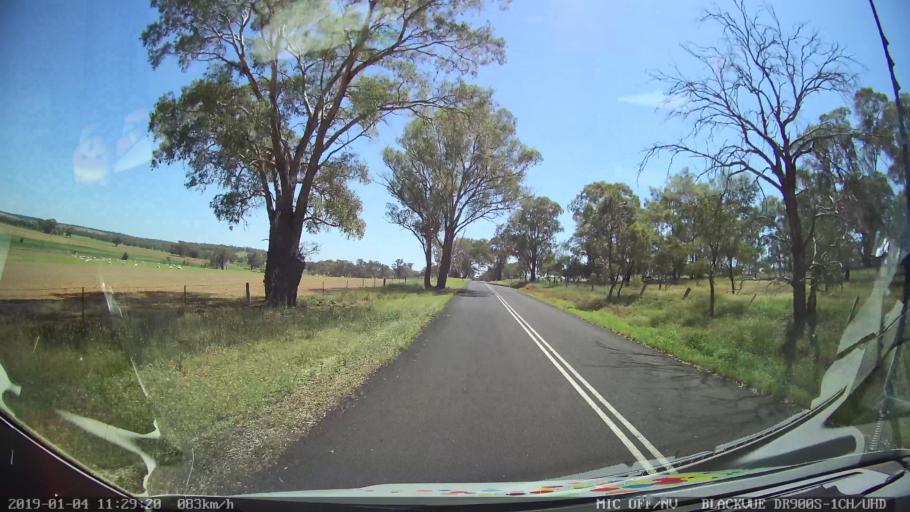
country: AU
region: New South Wales
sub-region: Cabonne
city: Molong
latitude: -33.0892
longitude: 148.7734
